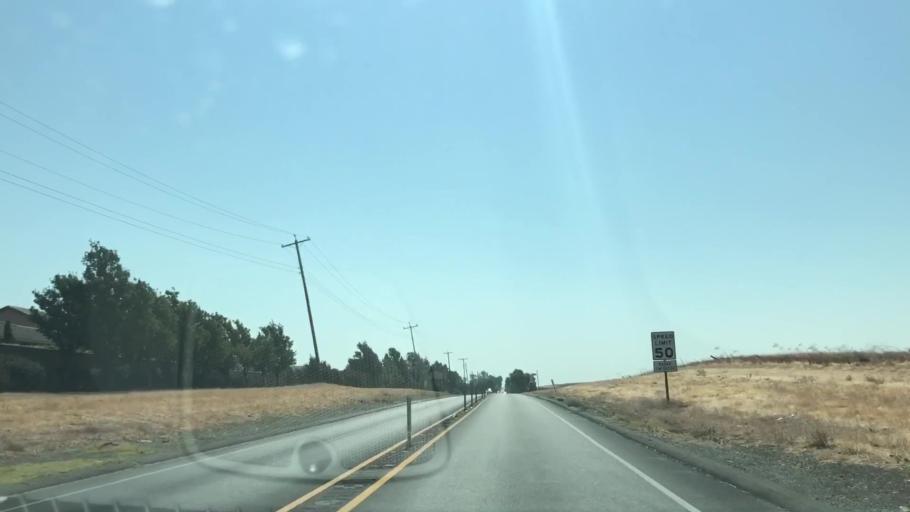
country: US
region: California
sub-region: Solano County
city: Rio Vista
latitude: 38.1798
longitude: -121.7209
